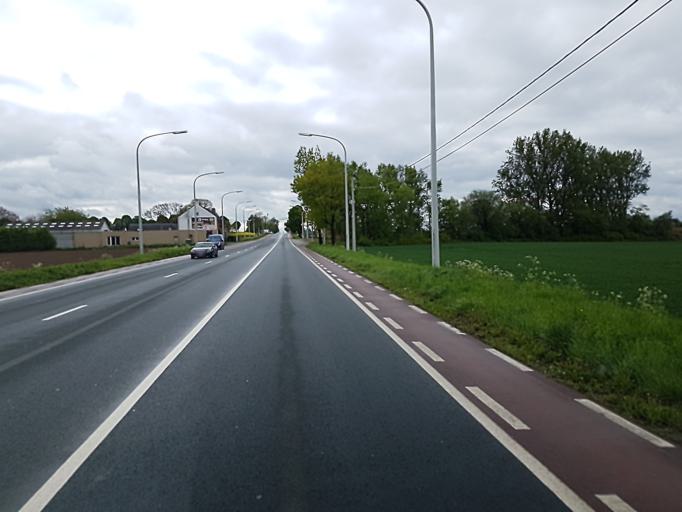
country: BE
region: Wallonia
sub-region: Province du Brabant Wallon
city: Chastre-Villeroux-Blanmont
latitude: 50.6159
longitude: 4.6638
